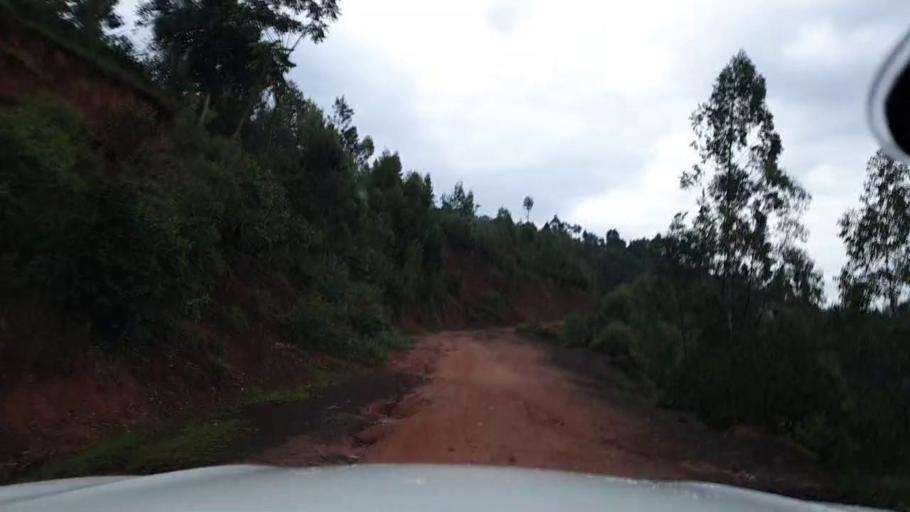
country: BI
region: Kayanza
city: Kayanza
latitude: -2.7199
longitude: 29.5452
